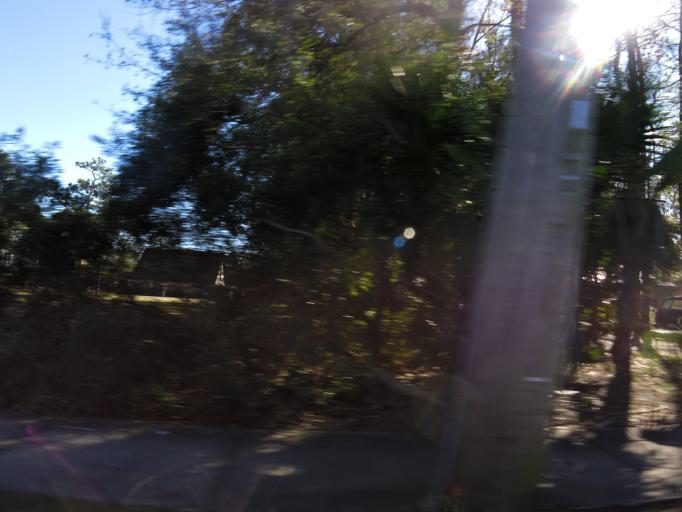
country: US
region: Florida
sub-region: Duval County
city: Jacksonville
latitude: 30.2845
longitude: -81.6101
